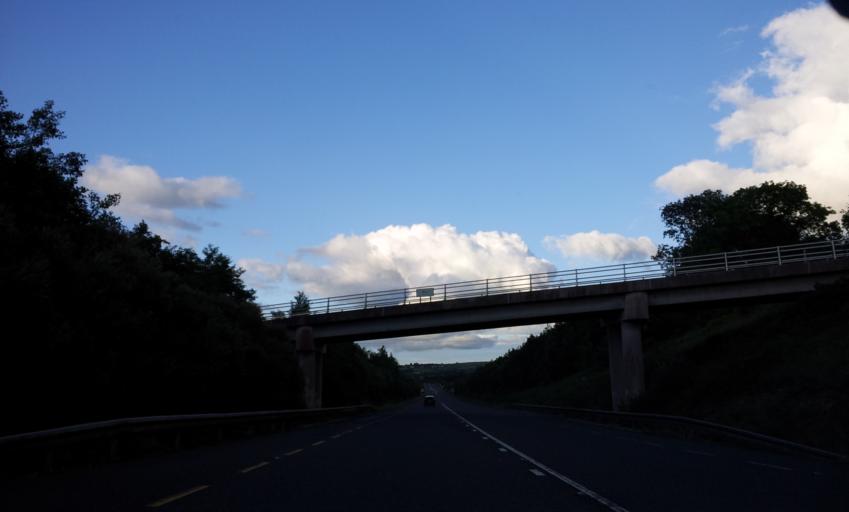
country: IE
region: Munster
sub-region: County Limerick
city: Abbeyfeale
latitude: 52.3407
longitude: -9.3496
